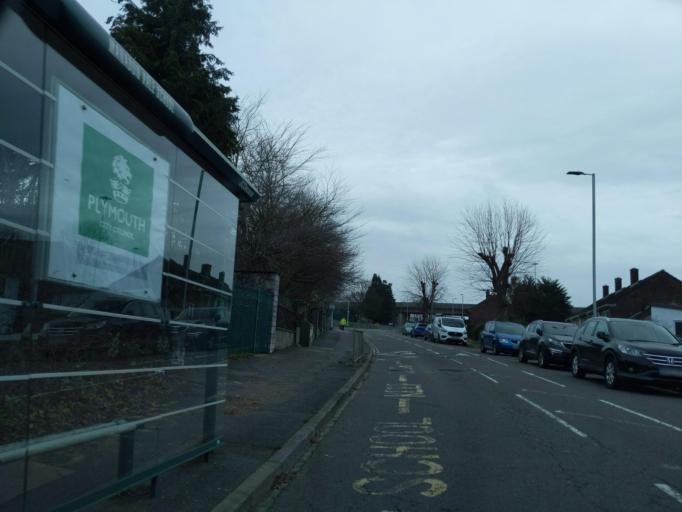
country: GB
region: England
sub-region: Plymouth
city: Plymouth
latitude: 50.4015
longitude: -4.1376
